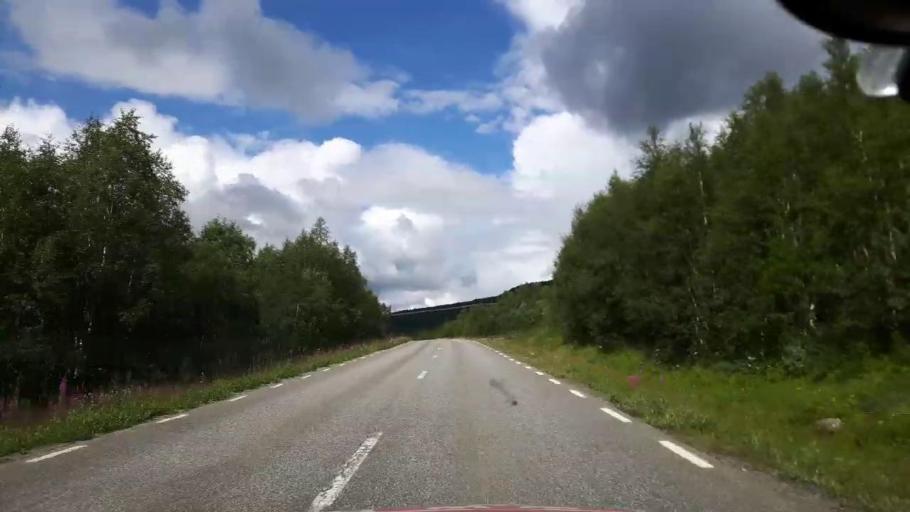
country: NO
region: Nordland
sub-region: Hattfjelldal
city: Hattfjelldal
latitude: 65.0593
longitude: 14.7158
